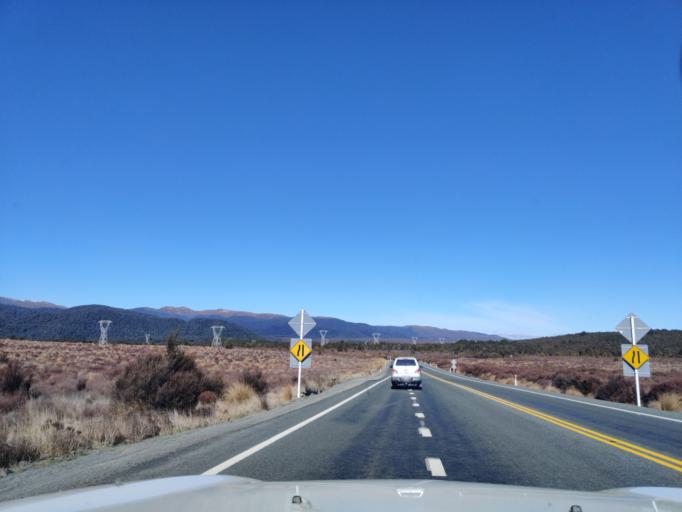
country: NZ
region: Waikato
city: Turangi
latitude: -39.1883
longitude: 175.7573
